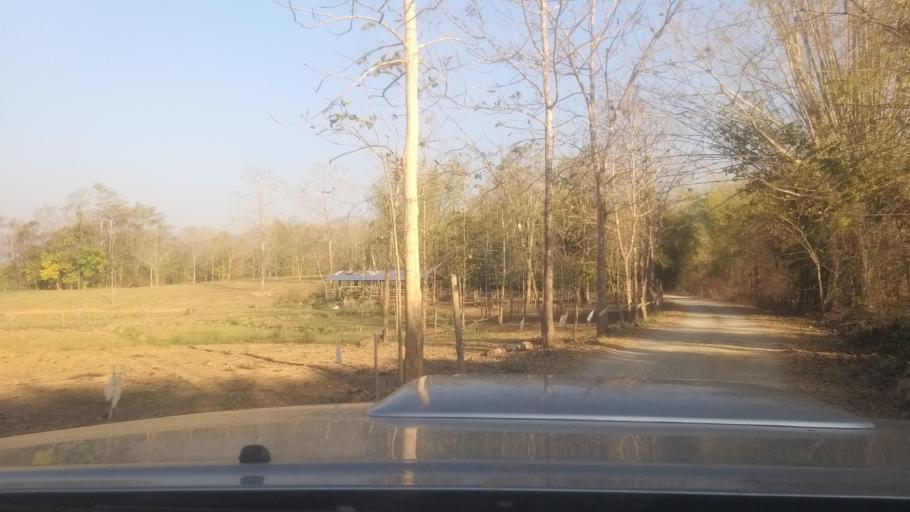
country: TH
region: Phrae
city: Phrae
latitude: 18.2623
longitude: 100.0122
